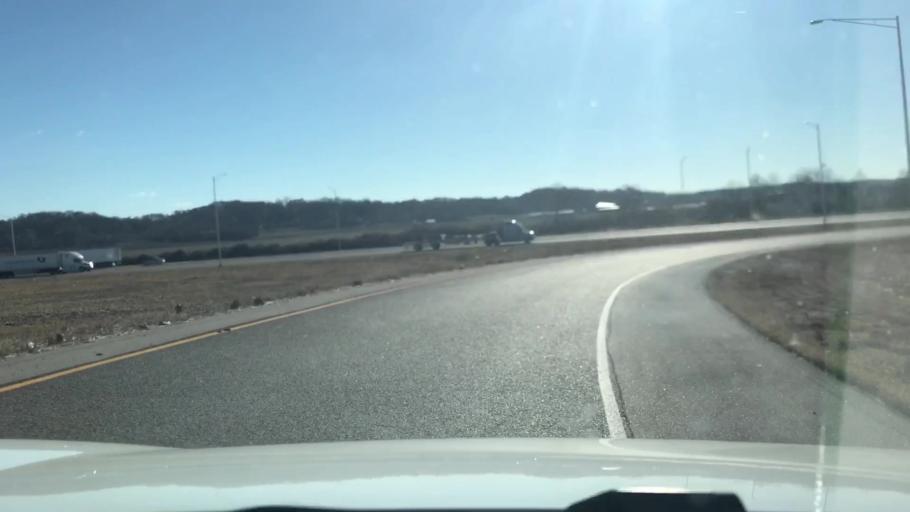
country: US
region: Illinois
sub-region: Saint Clair County
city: Caseyville
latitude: 38.6745
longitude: -90.0271
